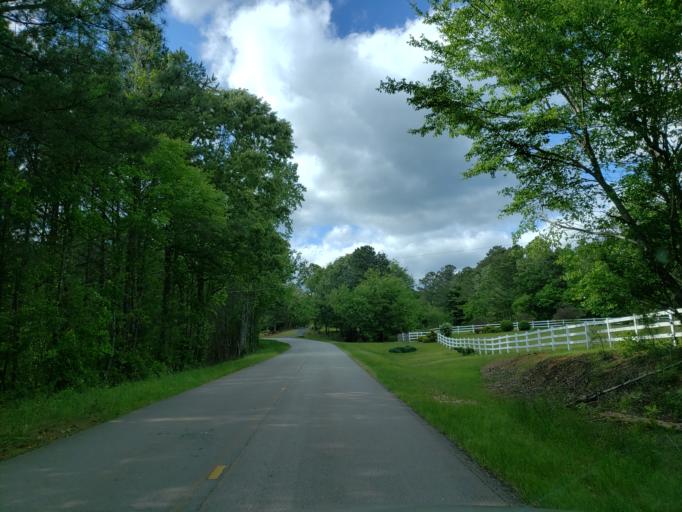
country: US
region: Georgia
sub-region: Carroll County
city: Mount Zion
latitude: 33.6452
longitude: -85.2791
